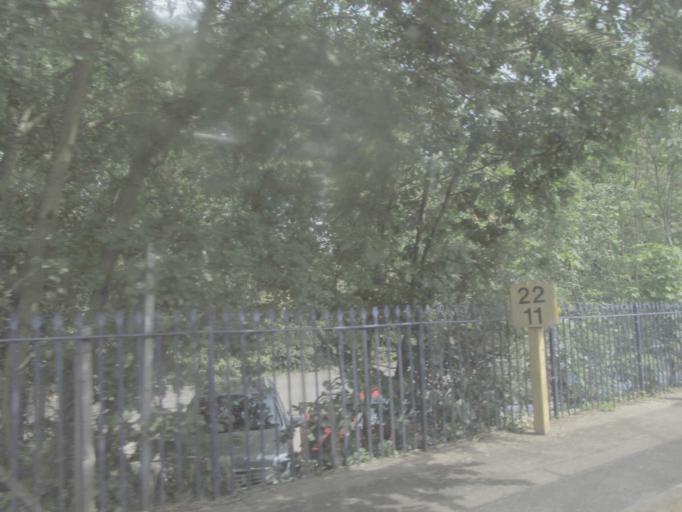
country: GB
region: England
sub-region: Royal Borough of Windsor and Maidenhead
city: Bray
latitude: 51.5233
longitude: -0.6832
